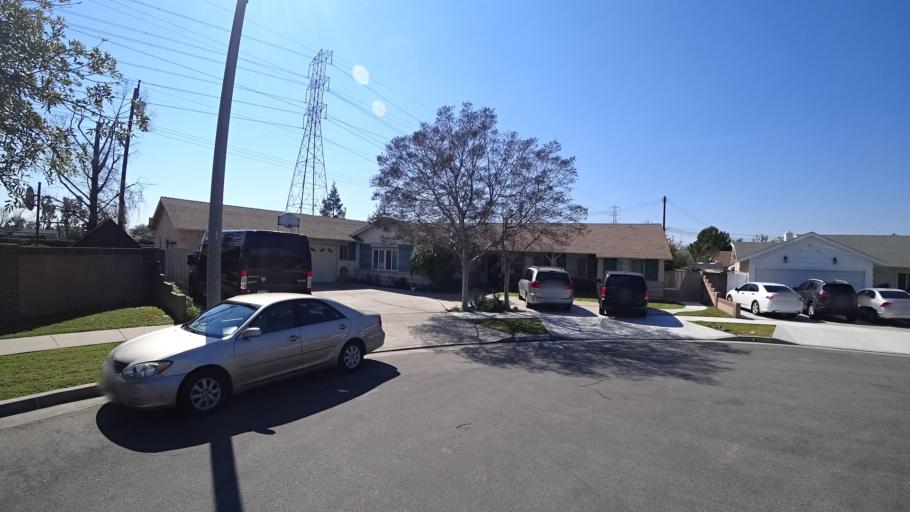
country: US
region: California
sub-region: Orange County
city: Garden Grove
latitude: 33.8076
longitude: -117.9512
